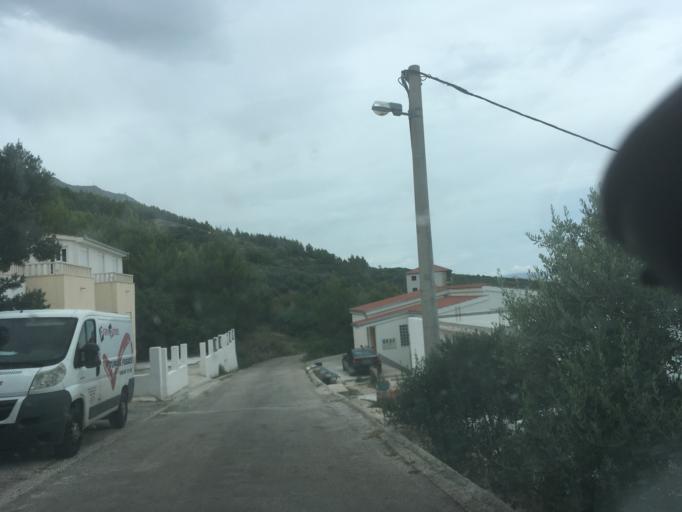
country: HR
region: Splitsko-Dalmatinska
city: Jesenice
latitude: 43.4578
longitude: 16.6196
